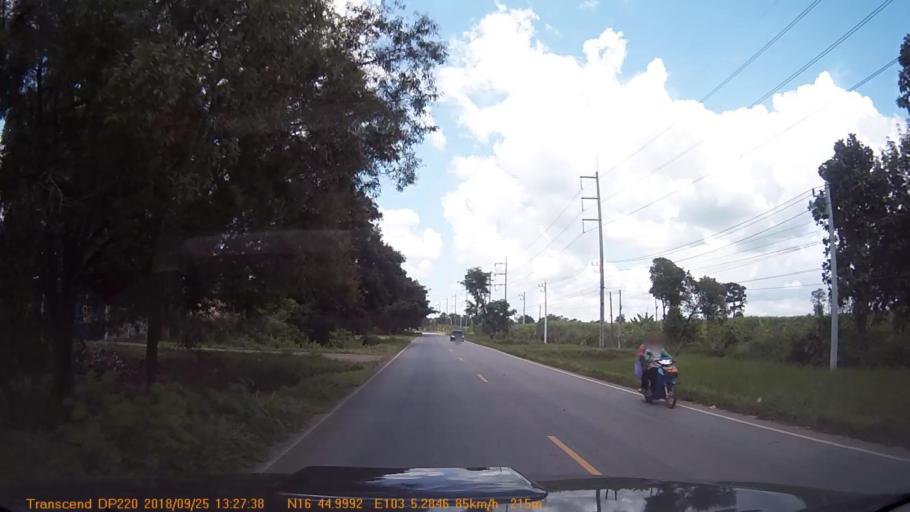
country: TH
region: Khon Kaen
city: Kranuan
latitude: 16.7500
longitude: 103.0881
